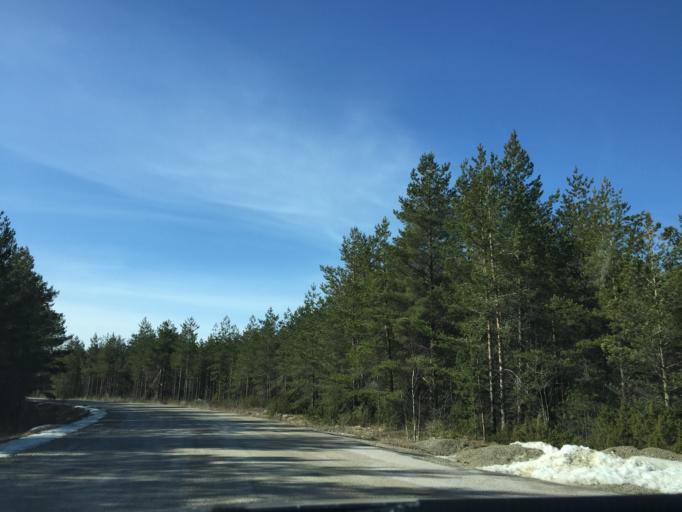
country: EE
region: Laeaene
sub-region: Lihula vald
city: Lihula
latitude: 58.6115
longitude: 23.5702
